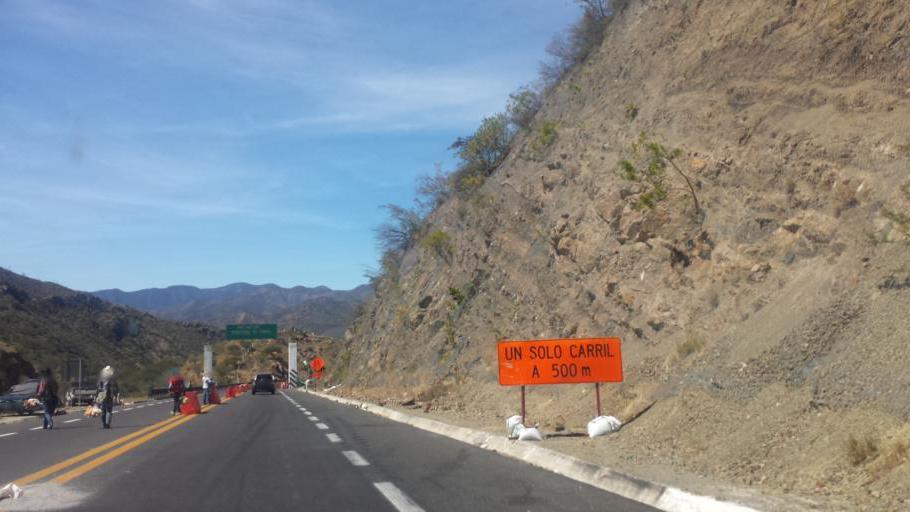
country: MX
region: Puebla
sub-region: San Jose Miahuatlan
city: San Pedro Tetitlan
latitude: 18.1072
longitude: -97.3399
